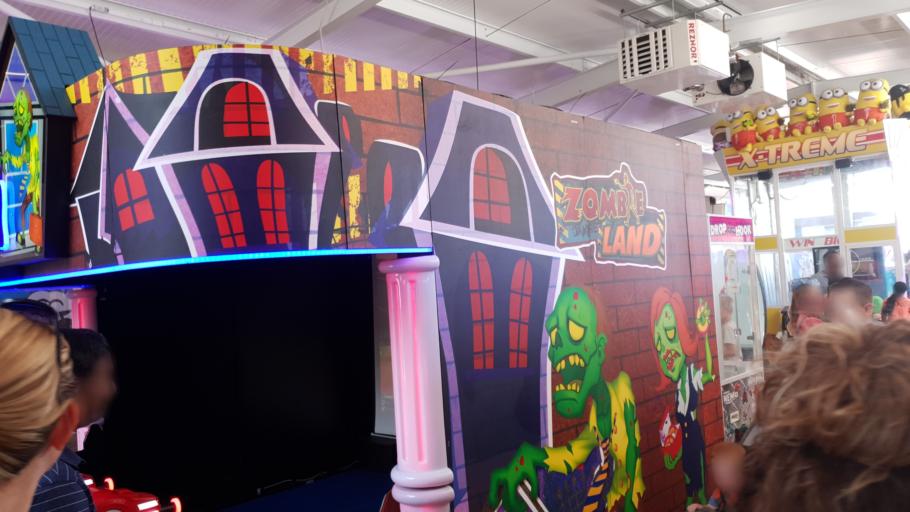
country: GB
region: England
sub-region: Essex
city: Clacton-on-Sea
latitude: 51.7864
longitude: 1.1552
